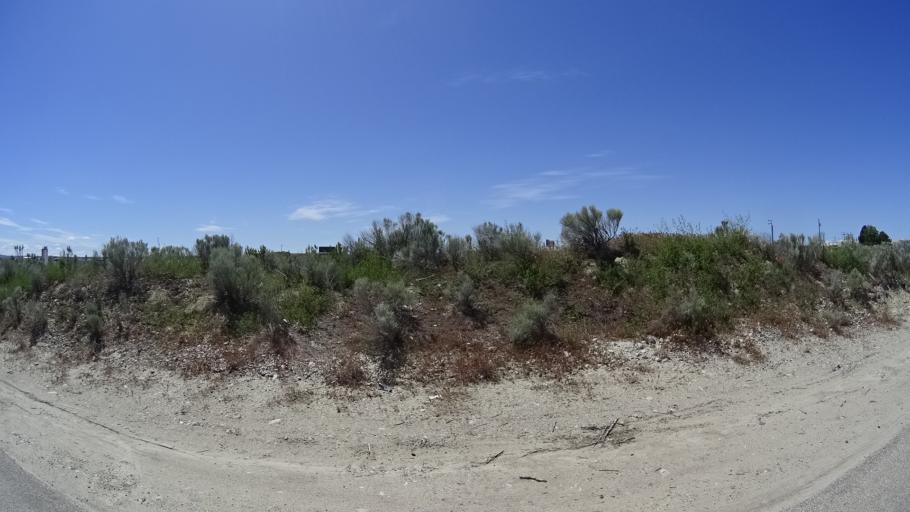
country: US
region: Idaho
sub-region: Ada County
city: Boise
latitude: 43.5604
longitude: -116.1827
